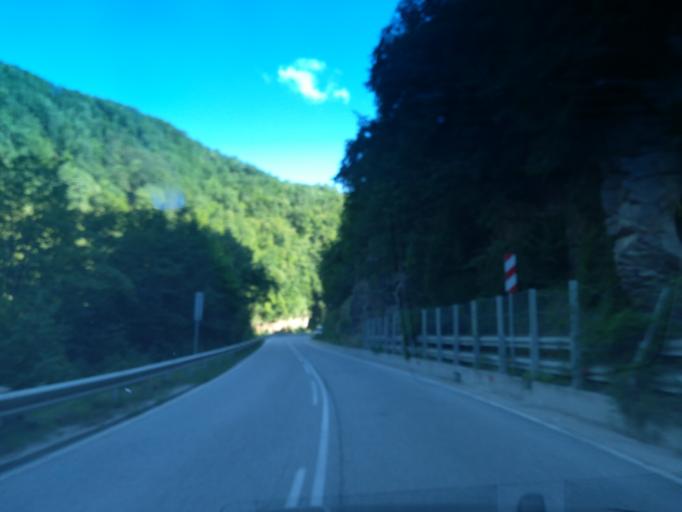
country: BG
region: Smolyan
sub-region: Obshtina Chepelare
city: Chepelare
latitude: 41.8001
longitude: 24.7099
